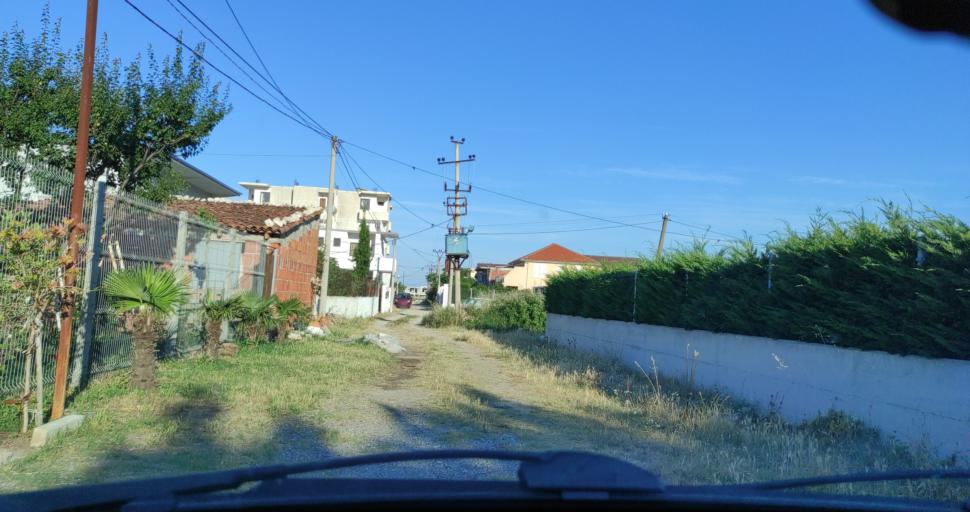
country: AL
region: Shkoder
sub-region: Rrethi i Shkodres
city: Velipoje
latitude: 41.8666
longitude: 19.4393
